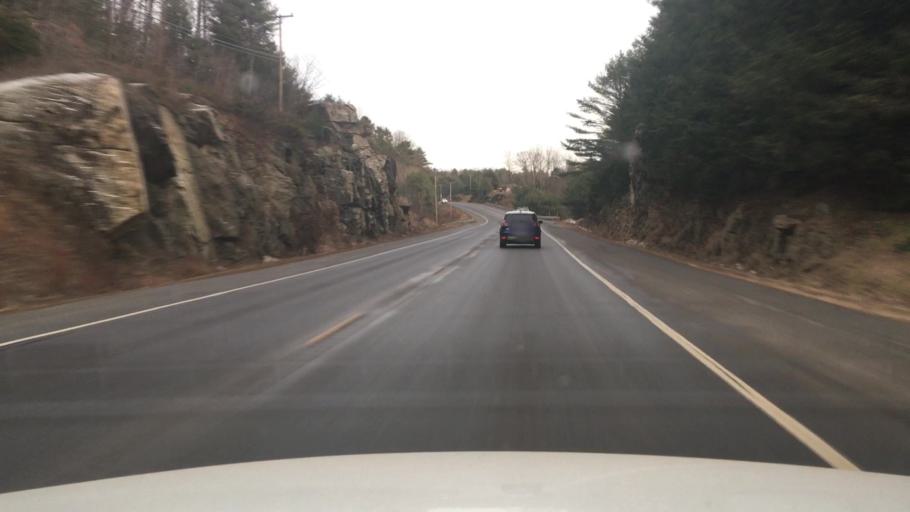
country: US
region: Maine
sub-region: Lincoln County
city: Wiscasset
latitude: 44.0021
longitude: -69.6228
